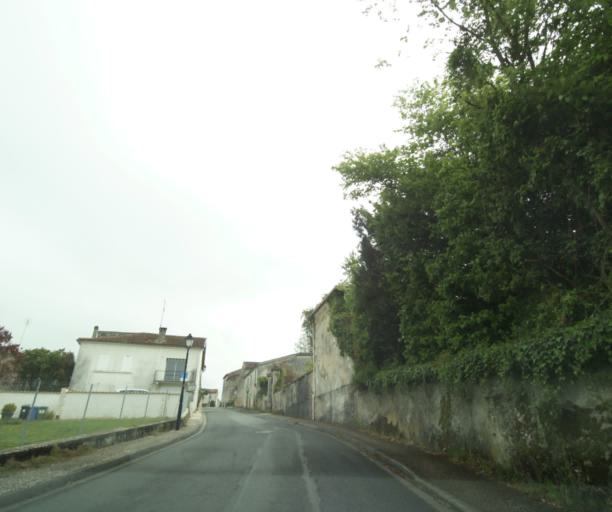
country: FR
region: Poitou-Charentes
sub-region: Departement de la Charente-Maritime
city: Chaniers
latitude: 45.7601
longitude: -0.5391
